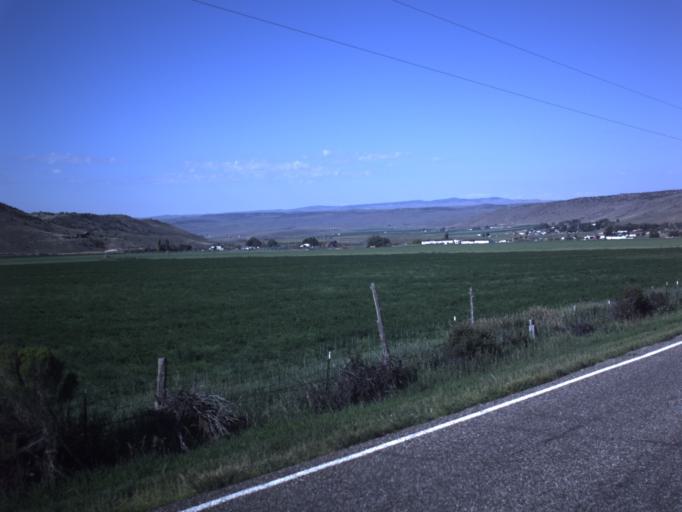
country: US
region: Utah
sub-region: Wayne County
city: Loa
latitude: 38.4694
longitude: -111.5840
